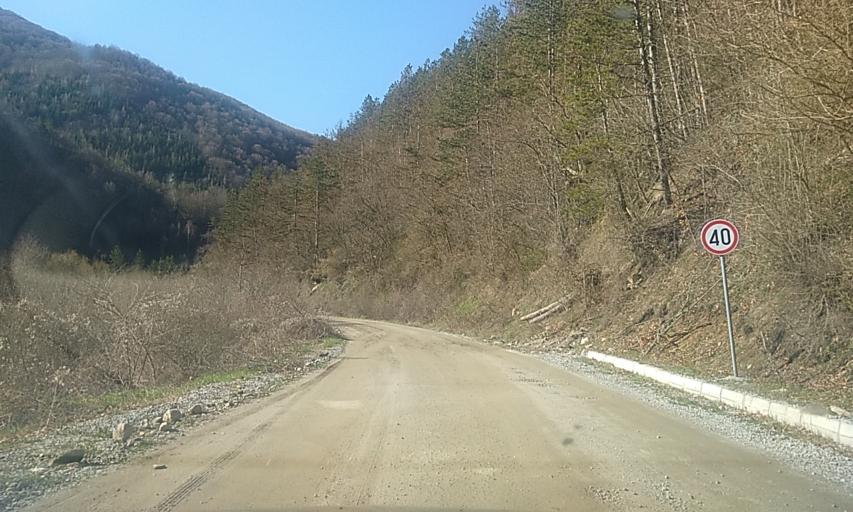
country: RS
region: Central Serbia
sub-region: Pcinjski Okrug
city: Bosilegrad
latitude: 42.3878
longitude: 22.4483
